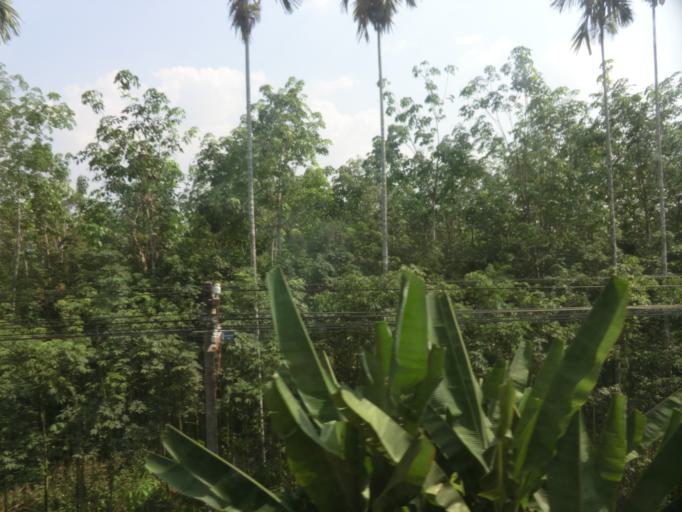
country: VN
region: Dong Nai
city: Long Khanh
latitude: 10.9301
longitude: 107.2105
